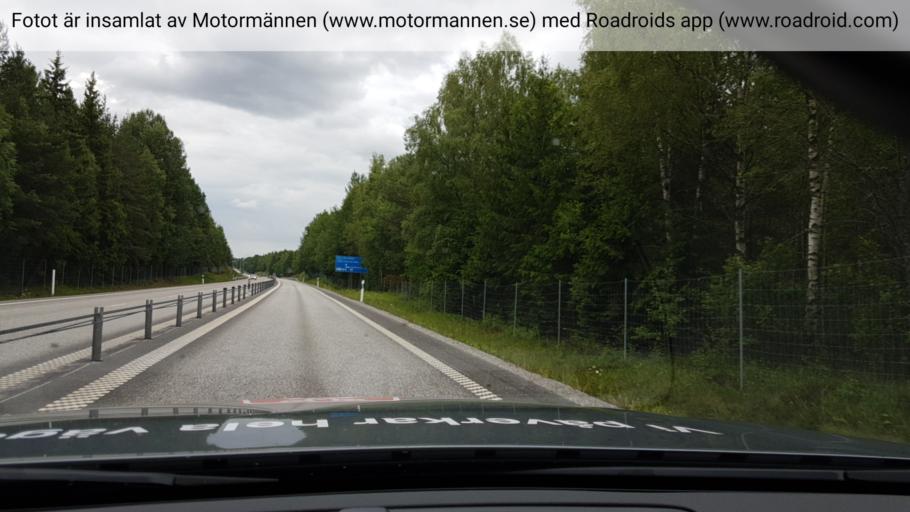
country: SE
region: Vaestmanland
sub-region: Surahammars Kommun
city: Surahammar
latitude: 59.7284
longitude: 16.2318
